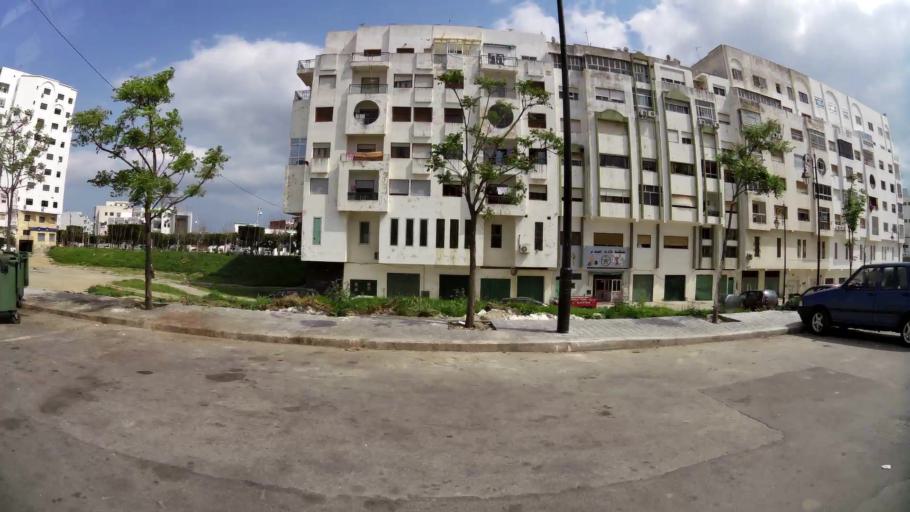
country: MA
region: Tanger-Tetouan
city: Tetouan
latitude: 35.5747
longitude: -5.3608
